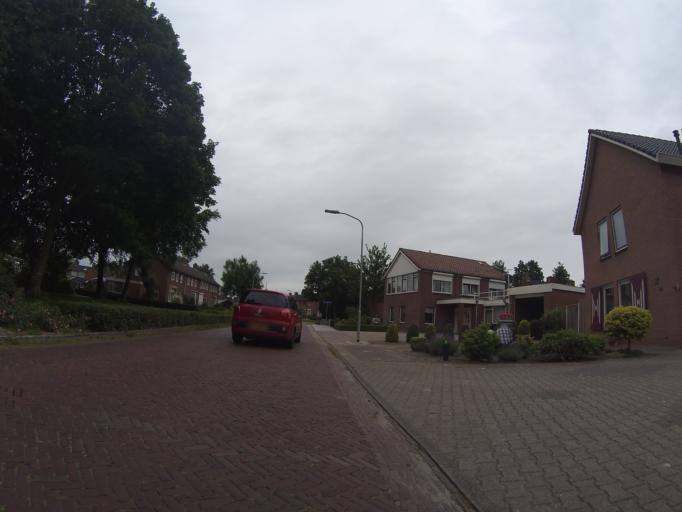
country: NL
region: Drenthe
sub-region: Gemeente Emmen
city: Emmer-Compascuum
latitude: 52.8125
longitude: 7.0501
